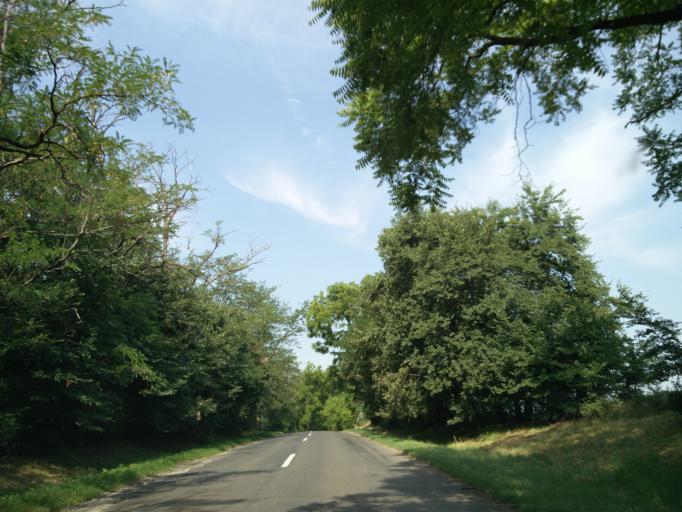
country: HU
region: Fejer
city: Bicske
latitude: 47.4325
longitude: 18.6234
